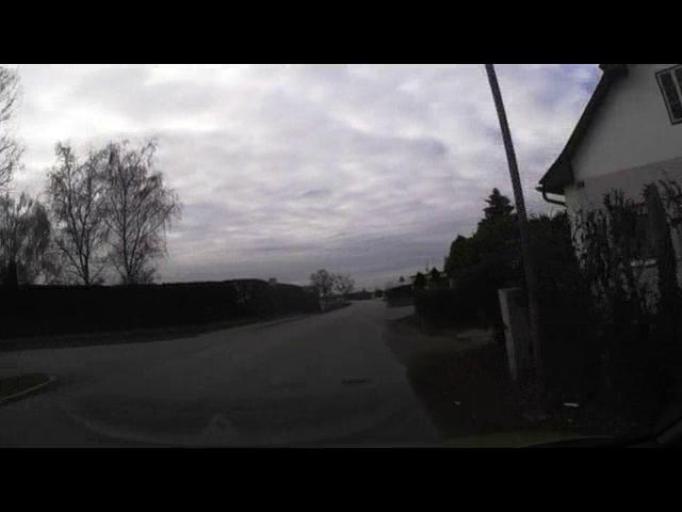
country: AT
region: Lower Austria
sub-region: Politischer Bezirk Baden
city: Pottendorf
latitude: 47.9104
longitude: 16.3799
